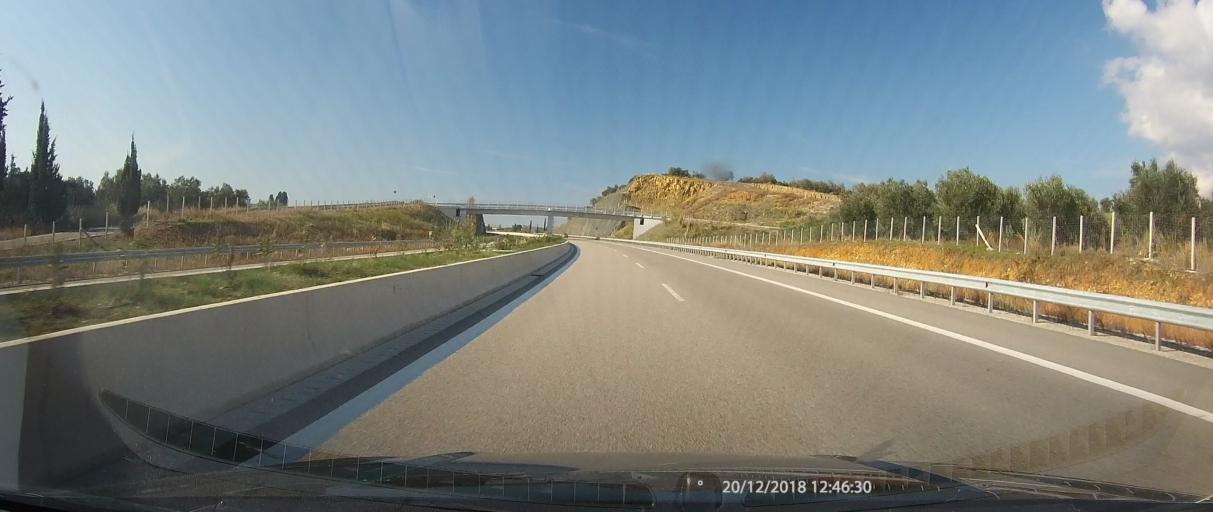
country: GR
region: West Greece
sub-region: Nomos Aitolias kai Akarnanias
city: Mesolongi
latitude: 38.3927
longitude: 21.4721
